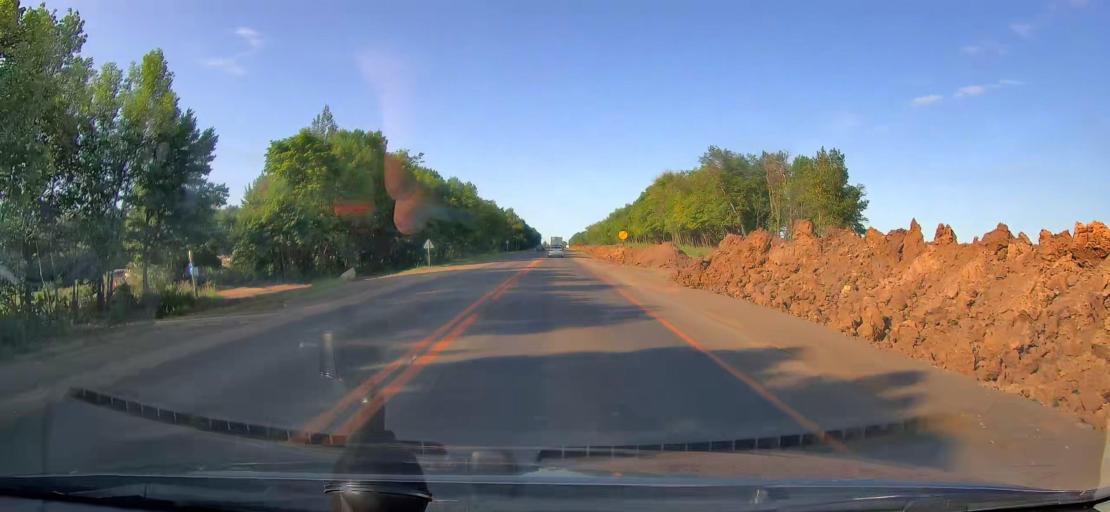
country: RU
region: Tula
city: Bol'shoye Skuratovo
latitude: 53.4099
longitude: 36.7745
